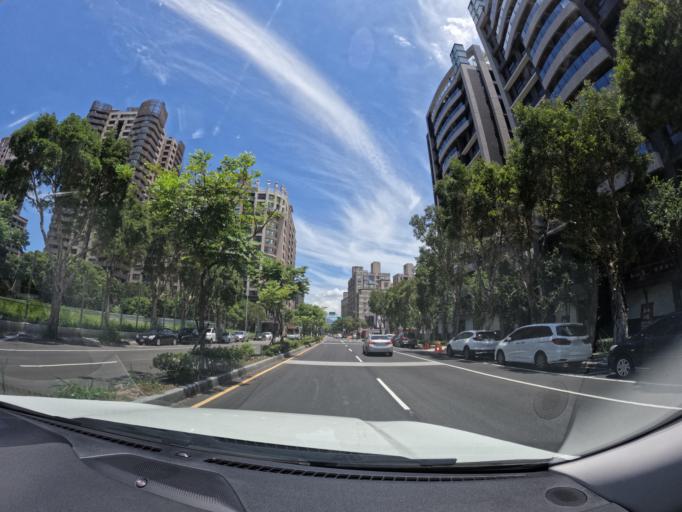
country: TW
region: Taiwan
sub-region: Taoyuan
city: Taoyuan
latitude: 25.0801
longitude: 121.3776
